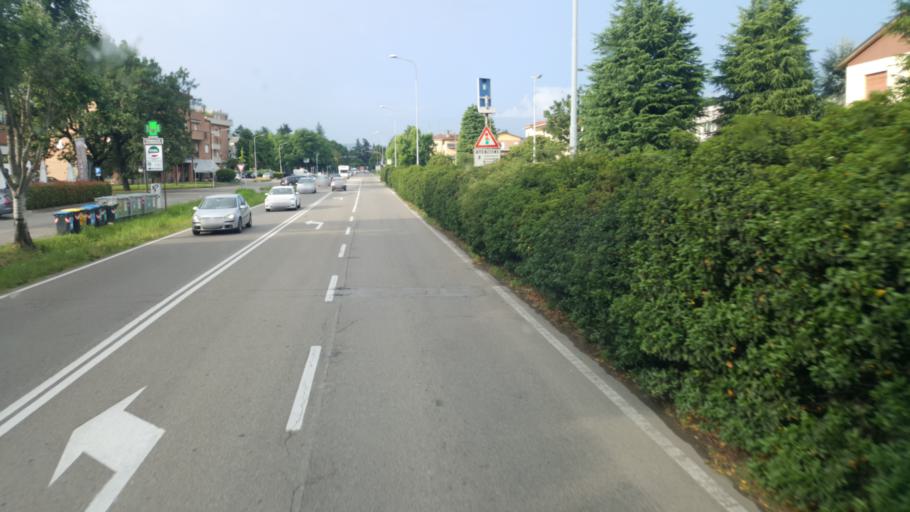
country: IT
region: Emilia-Romagna
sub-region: Provincia di Modena
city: Vignola
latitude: 44.4866
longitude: 10.9982
